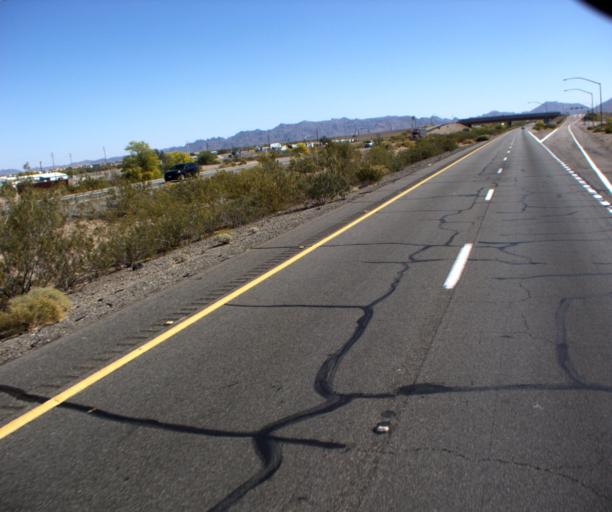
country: US
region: Arizona
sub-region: La Paz County
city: Quartzsite
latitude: 33.6645
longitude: -114.2062
